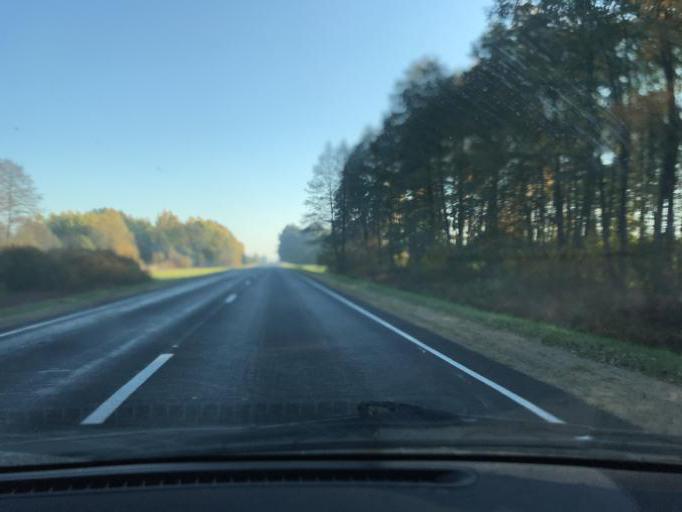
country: BY
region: Brest
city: Baranovichi
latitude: 52.8881
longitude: 25.8088
